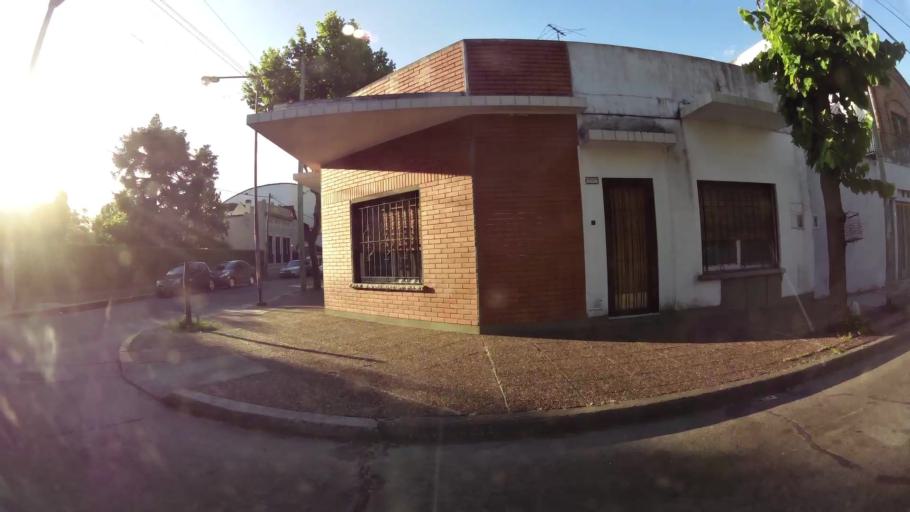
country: AR
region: Buenos Aires
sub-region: Partido de General San Martin
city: General San Martin
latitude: -34.5648
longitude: -58.5429
